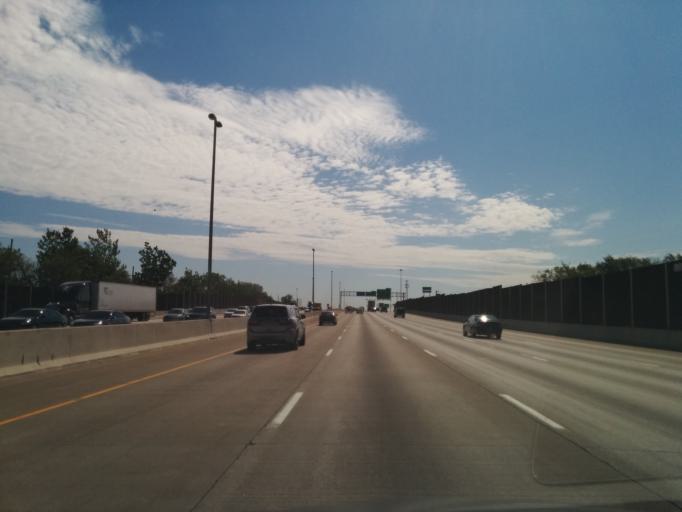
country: US
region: Indiana
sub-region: Lake County
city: Hammond
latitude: 41.5742
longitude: -87.4890
